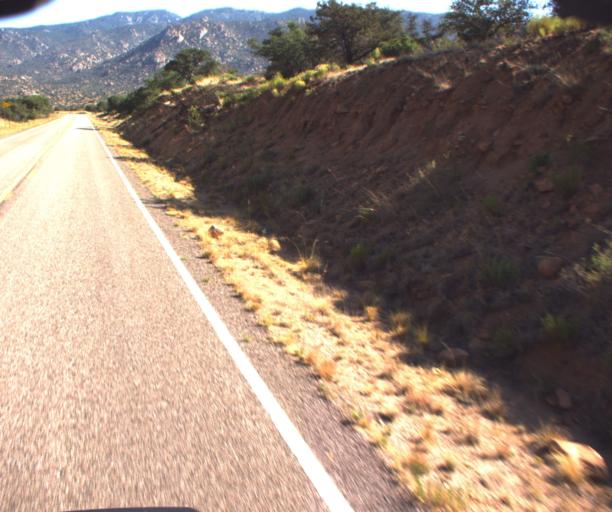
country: US
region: Arizona
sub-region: Graham County
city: Swift Trail Junction
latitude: 32.5871
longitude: -109.8543
